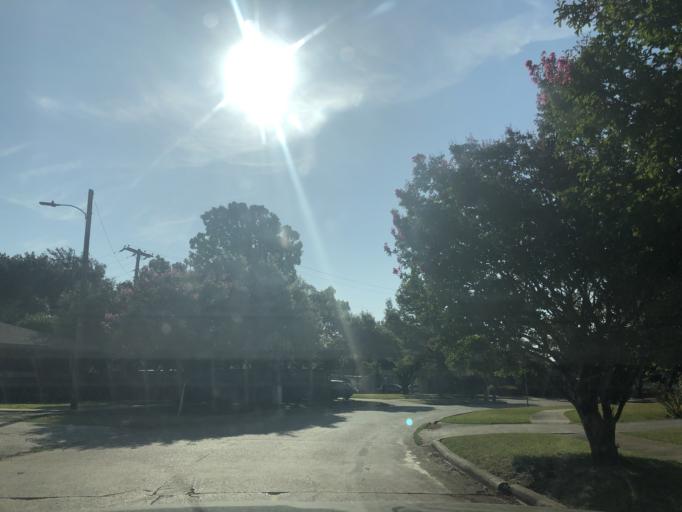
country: US
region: Texas
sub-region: Dallas County
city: Garland
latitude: 32.8682
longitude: -96.6368
